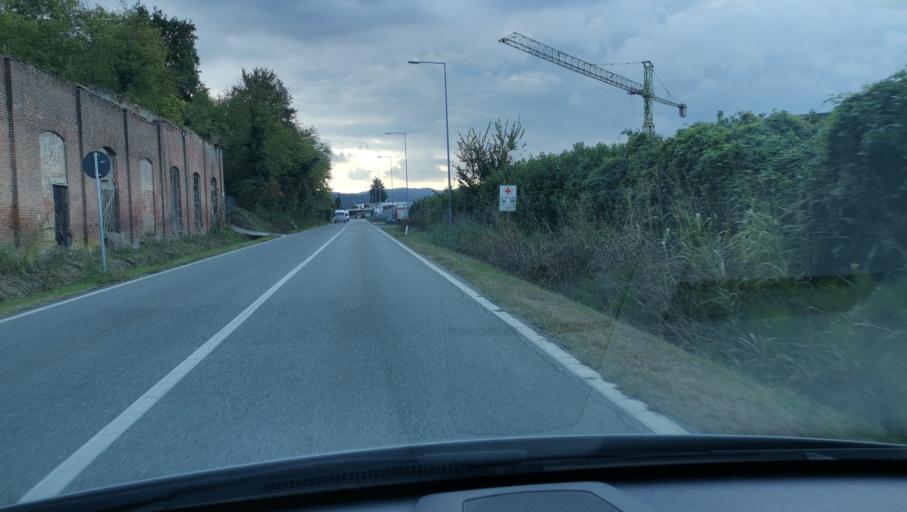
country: IT
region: Piedmont
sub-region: Provincia di Torino
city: Piana San Raffaele
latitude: 45.1611
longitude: 7.8544
